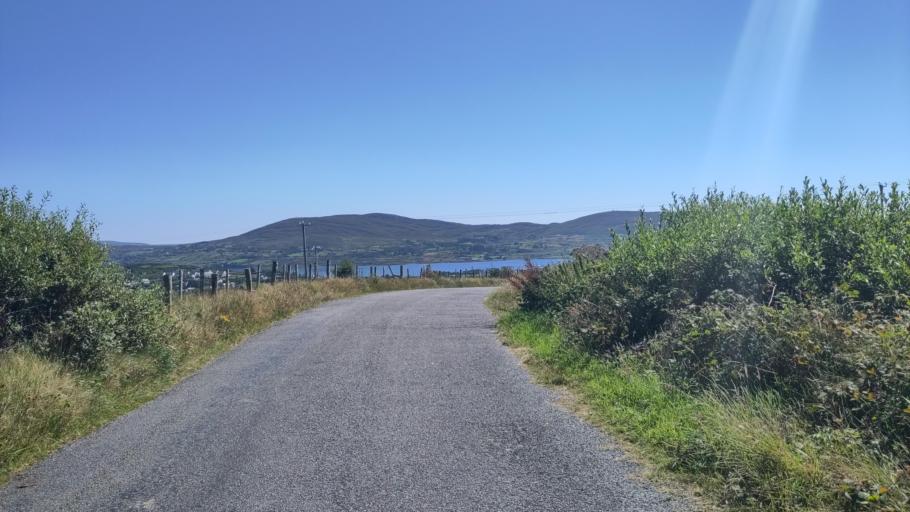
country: IE
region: Munster
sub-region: Ciarrai
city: Kenmare
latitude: 51.6659
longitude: -9.9104
